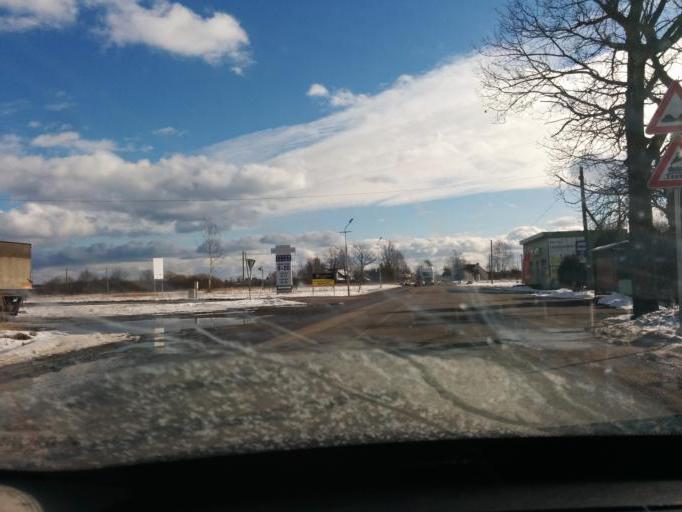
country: LV
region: Gulbenes Rajons
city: Gulbene
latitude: 57.1806
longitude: 26.7401
